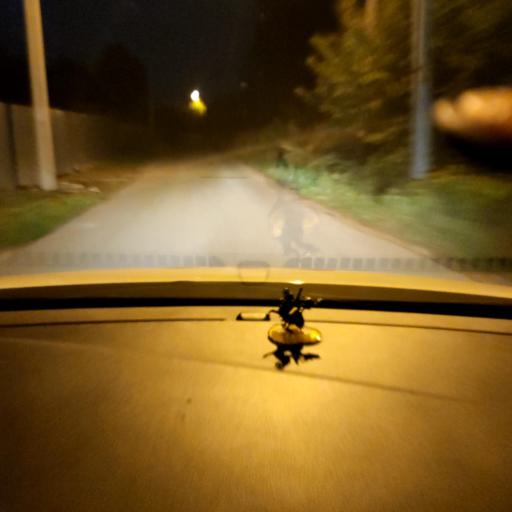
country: RU
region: Tatarstan
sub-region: Gorod Kazan'
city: Kazan
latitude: 55.7343
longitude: 49.0914
